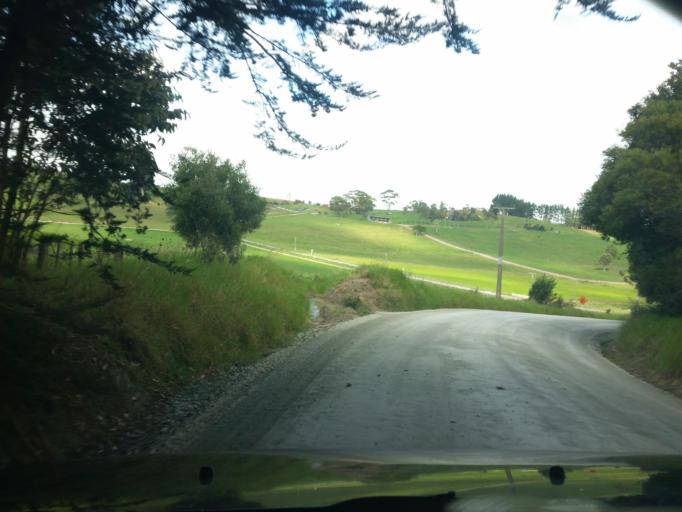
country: NZ
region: Northland
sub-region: Kaipara District
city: Dargaville
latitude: -35.9995
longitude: 173.9481
